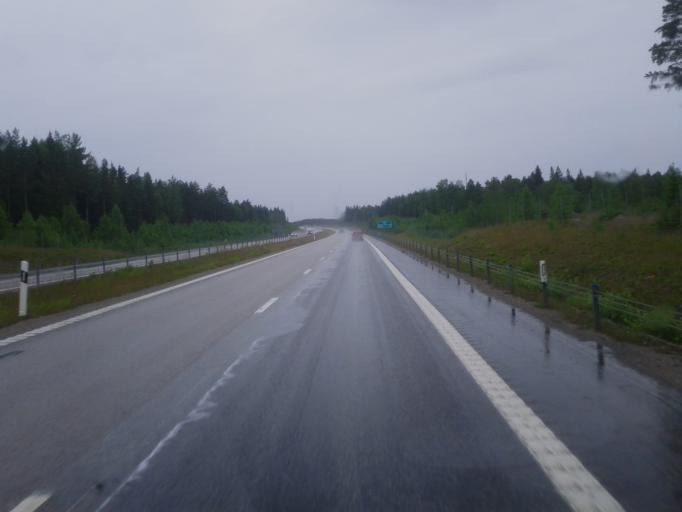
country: SE
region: Uppsala
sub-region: Tierps Kommun
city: Tierp
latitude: 60.2285
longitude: 17.5003
